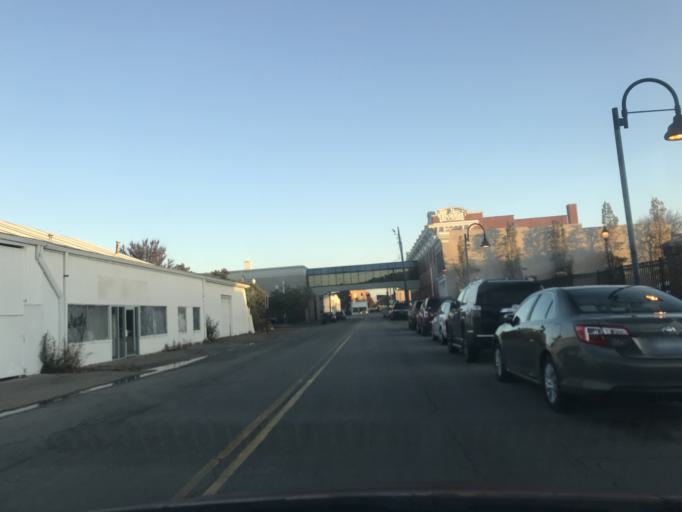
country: US
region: Indiana
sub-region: Clark County
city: Jeffersonville
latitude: 38.2527
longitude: -85.7315
